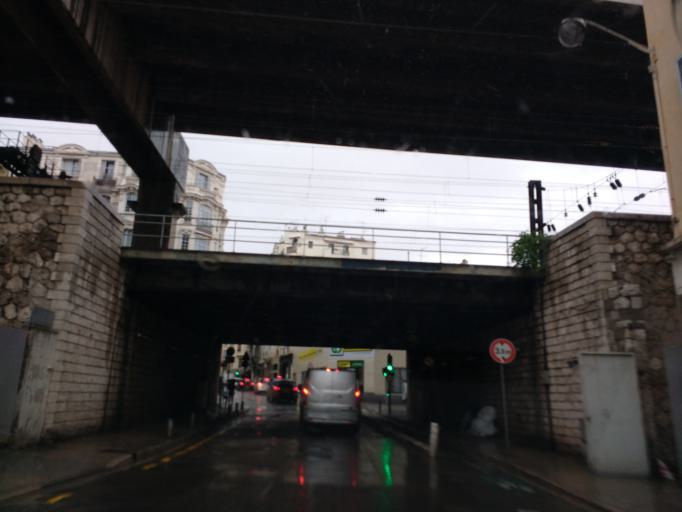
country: FR
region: Provence-Alpes-Cote d'Azur
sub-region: Departement des Alpes-Maritimes
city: Nice
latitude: 43.7067
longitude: 7.2668
